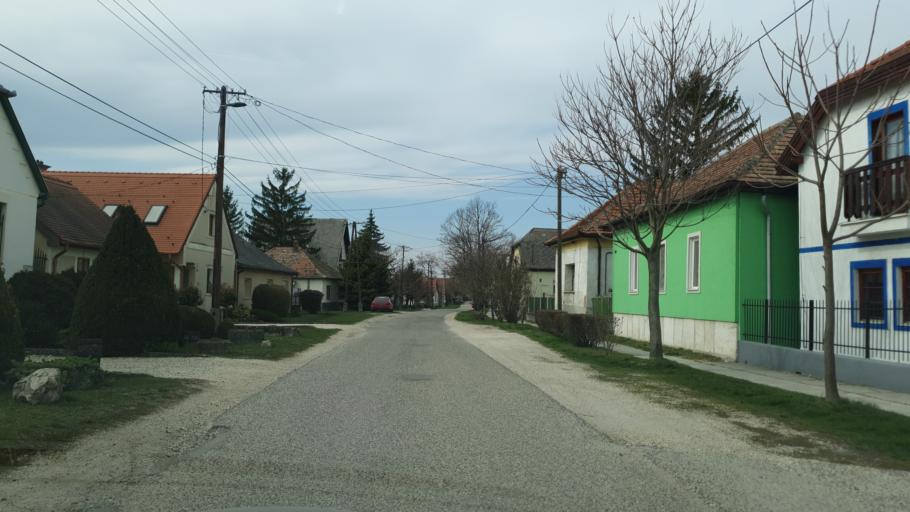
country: HU
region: Fejer
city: Etyek
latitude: 47.4465
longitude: 18.7496
